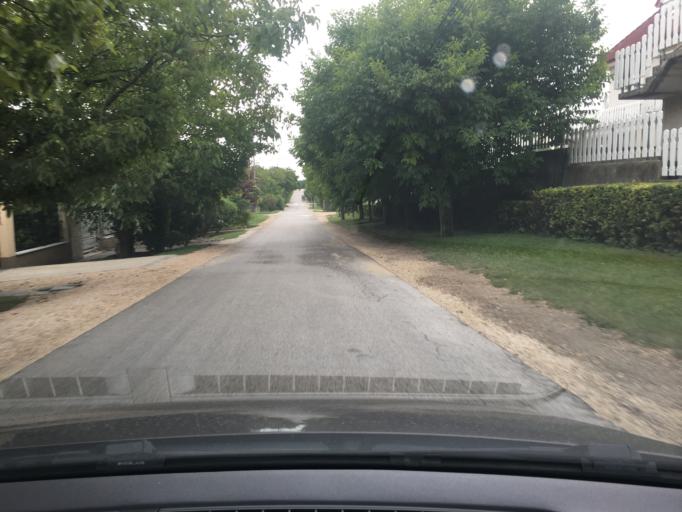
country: HU
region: Pest
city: Erd
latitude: 47.3924
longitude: 18.9026
